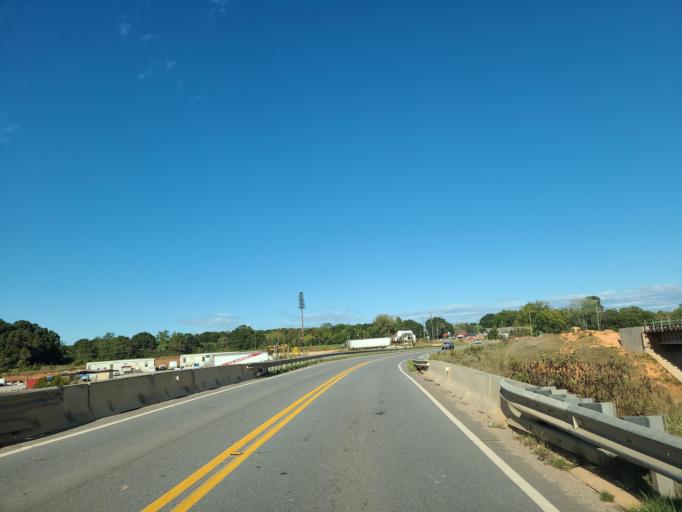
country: US
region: North Carolina
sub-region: Cleveland County
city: Shelby
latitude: 35.3254
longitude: -81.5129
